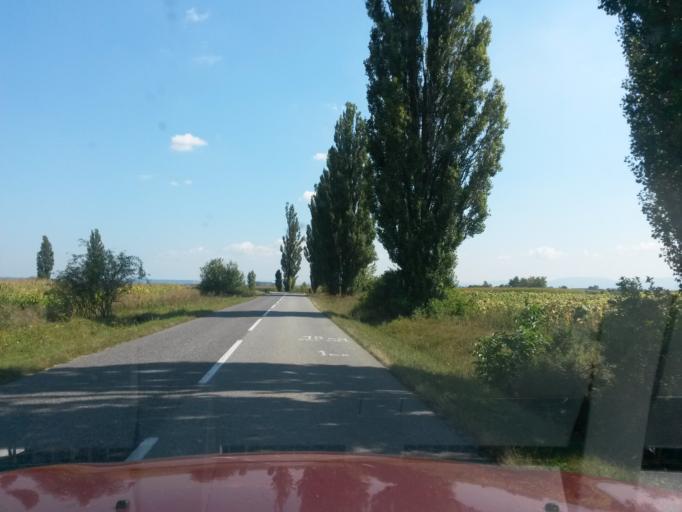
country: SK
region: Kosicky
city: Moldava nad Bodvou
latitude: 48.5481
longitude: 21.0827
